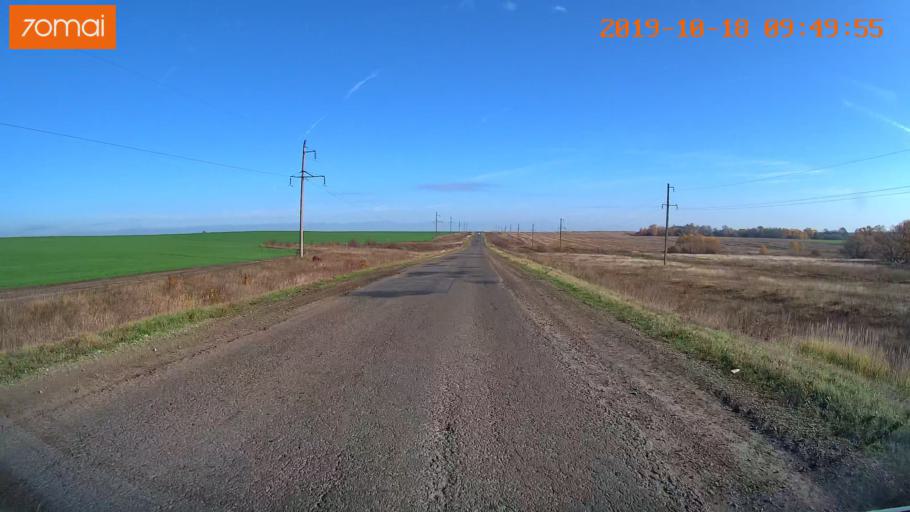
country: RU
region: Tula
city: Kazachka
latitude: 53.3231
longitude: 38.2704
